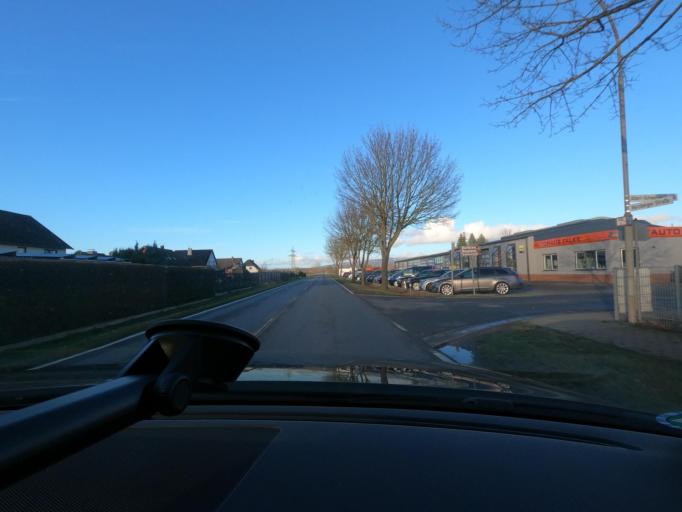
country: DE
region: Lower Saxony
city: Rhumspringe
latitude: 51.6133
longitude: 10.3223
